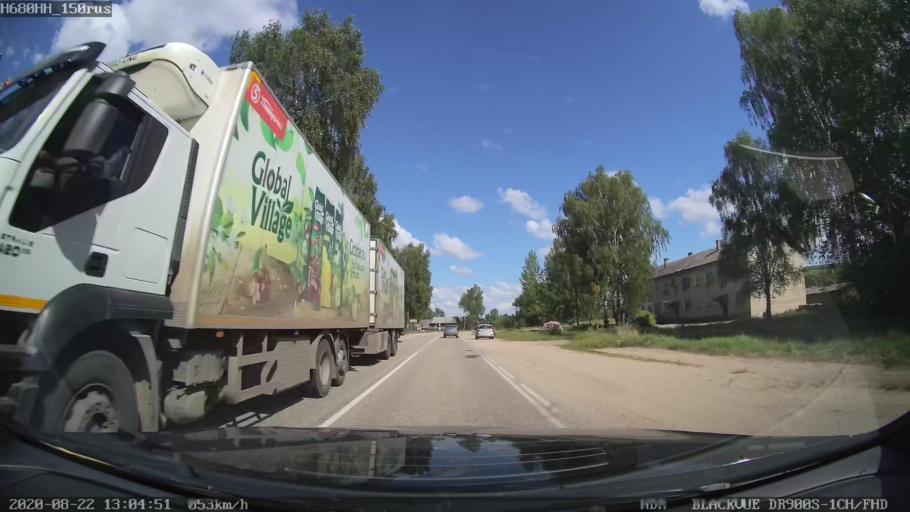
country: RU
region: Tverskaya
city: Bezhetsk
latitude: 57.6689
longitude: 36.4378
